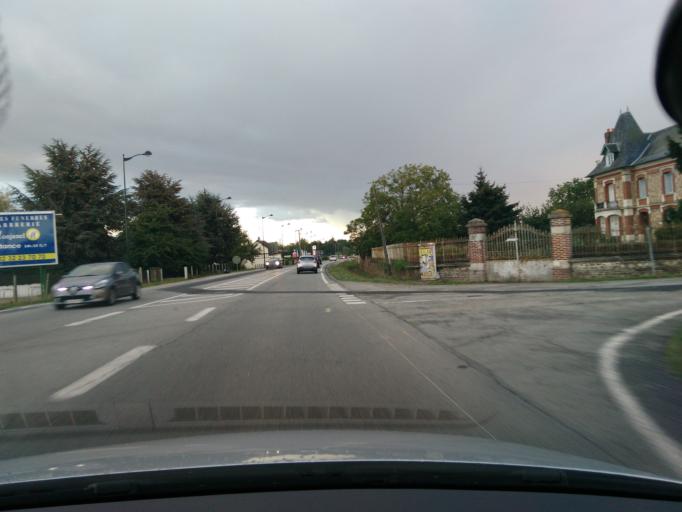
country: FR
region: Haute-Normandie
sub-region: Departement de l'Eure
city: Evreux
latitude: 48.9977
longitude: 1.1551
